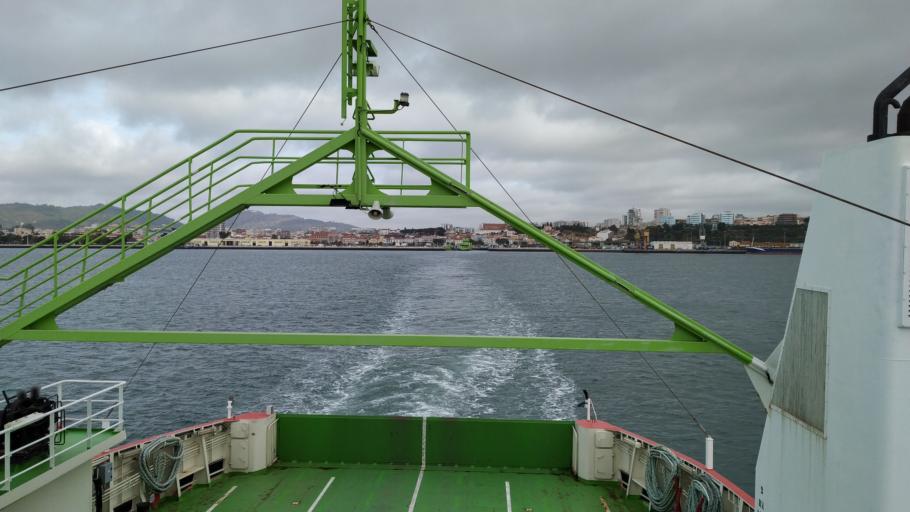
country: PT
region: Setubal
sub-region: Setubal
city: Setubal
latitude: 38.5124
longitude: -8.8865
